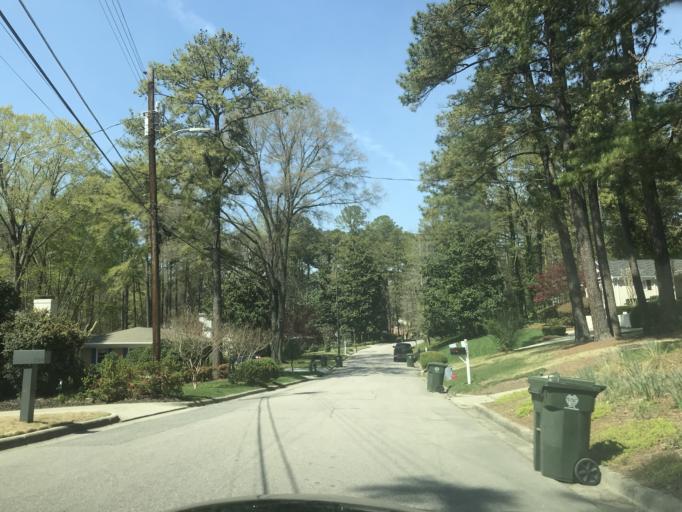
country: US
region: North Carolina
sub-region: Wake County
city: West Raleigh
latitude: 35.8264
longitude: -78.6368
